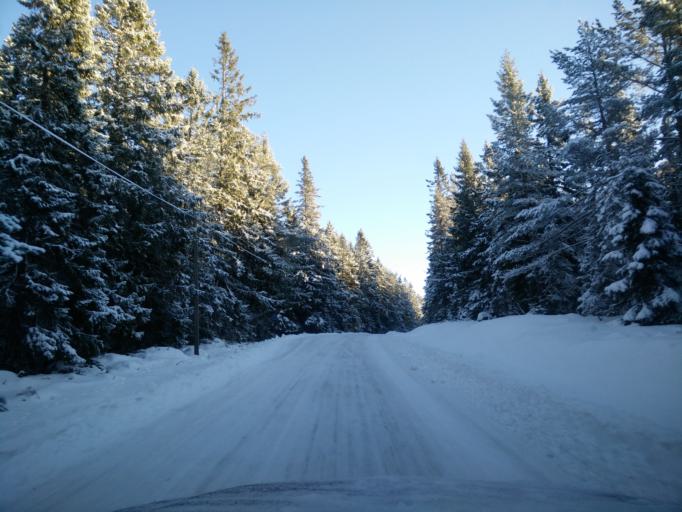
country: SE
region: Vaesternorrland
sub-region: Sundsvalls Kommun
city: Njurundabommen
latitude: 62.2357
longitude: 17.6130
